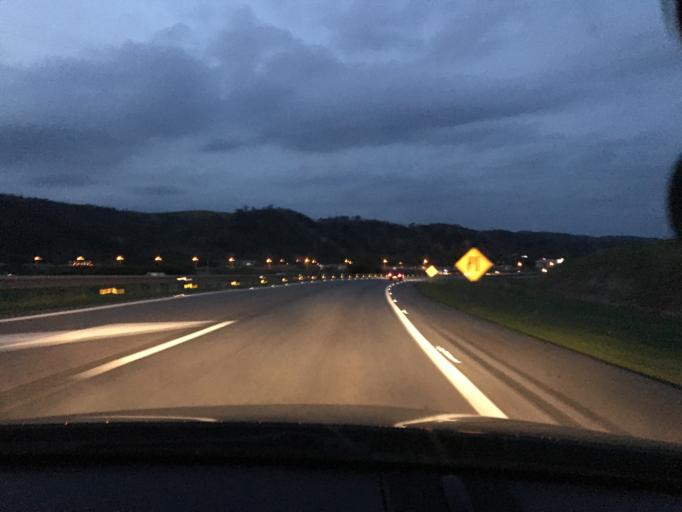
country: BR
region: Sao Paulo
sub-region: Santa Isabel
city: Santa Isabel
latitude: -23.3324
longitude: -46.1324
